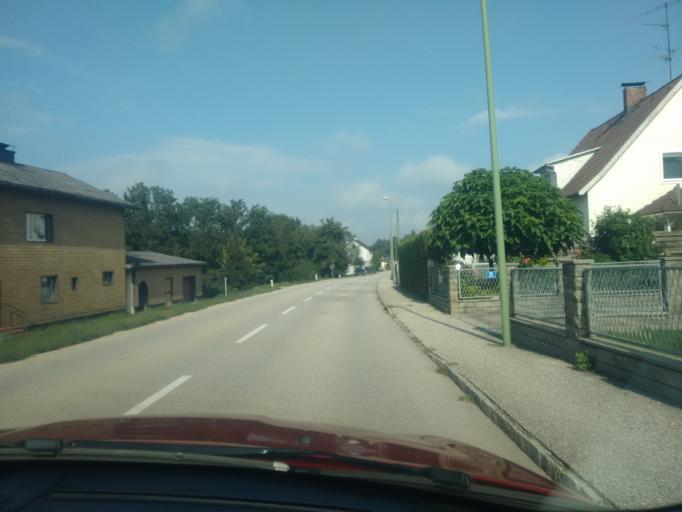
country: AT
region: Upper Austria
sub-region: Wels-Land
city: Steinhaus
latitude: 48.1310
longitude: 14.0103
